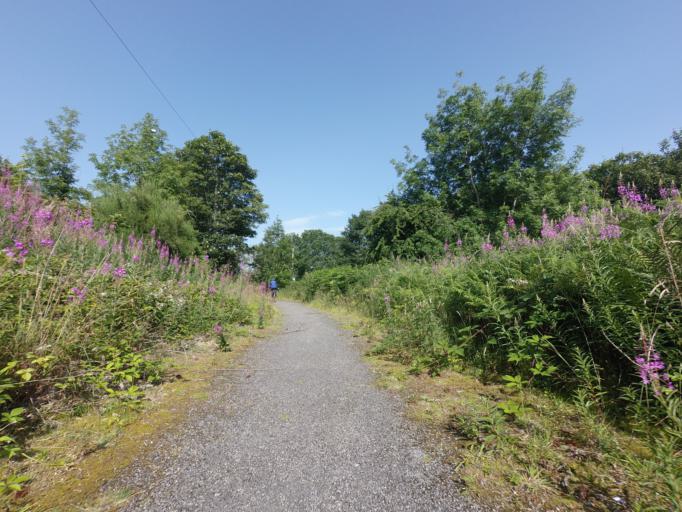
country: GB
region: Scotland
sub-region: Highland
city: Evanton
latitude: 57.6665
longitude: -4.3283
